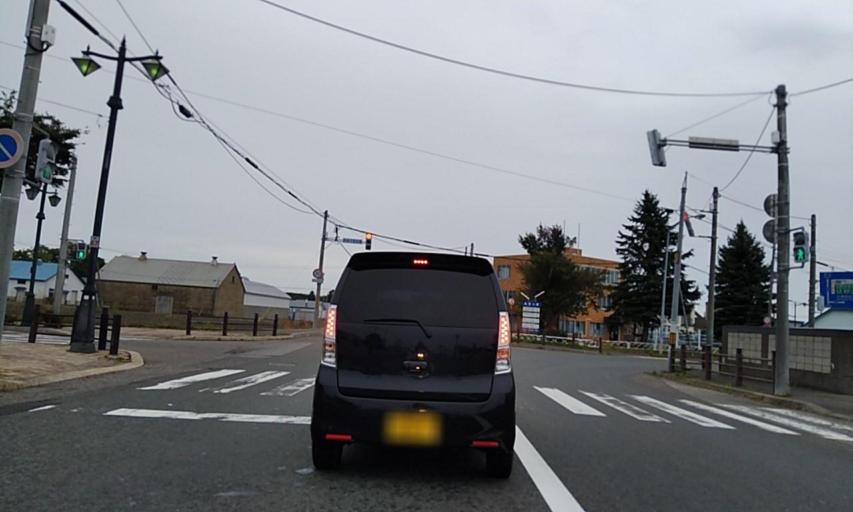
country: JP
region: Hokkaido
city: Bihoro
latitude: 43.9147
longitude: 144.1726
